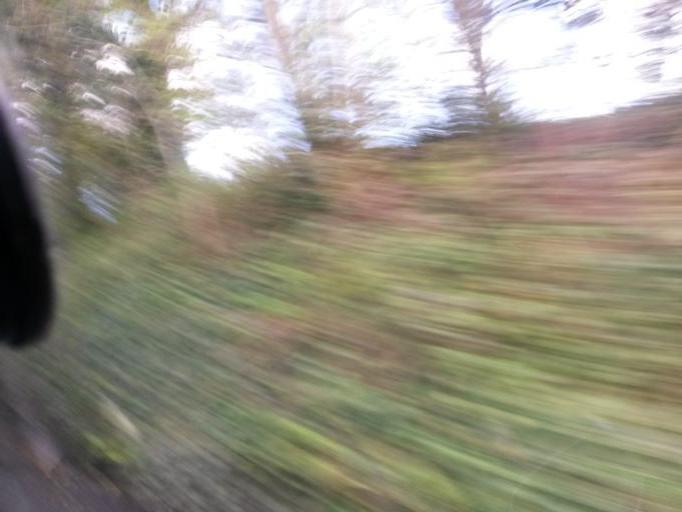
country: IE
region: Munster
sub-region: Waterford
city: Waterford
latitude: 52.2344
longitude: -7.0306
